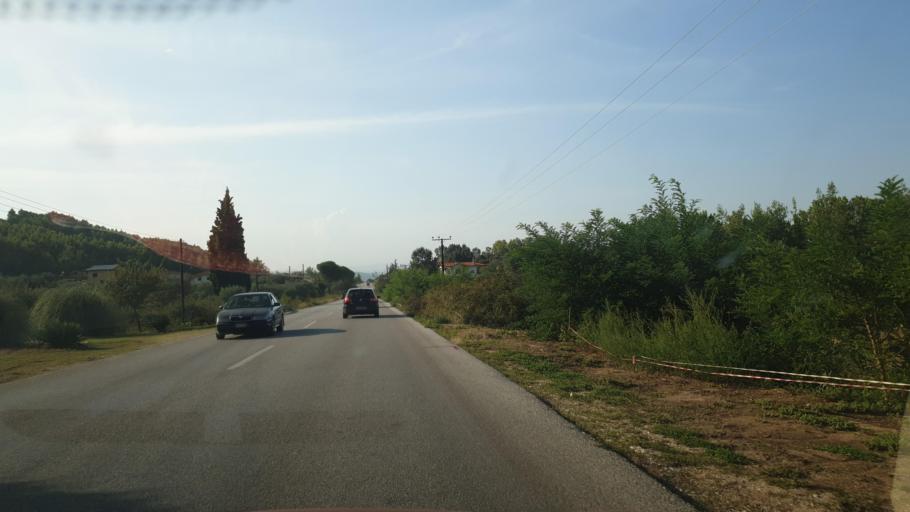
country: GR
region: Central Macedonia
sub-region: Nomos Chalkidikis
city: Agios Nikolaos
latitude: 40.2198
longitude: 23.7493
